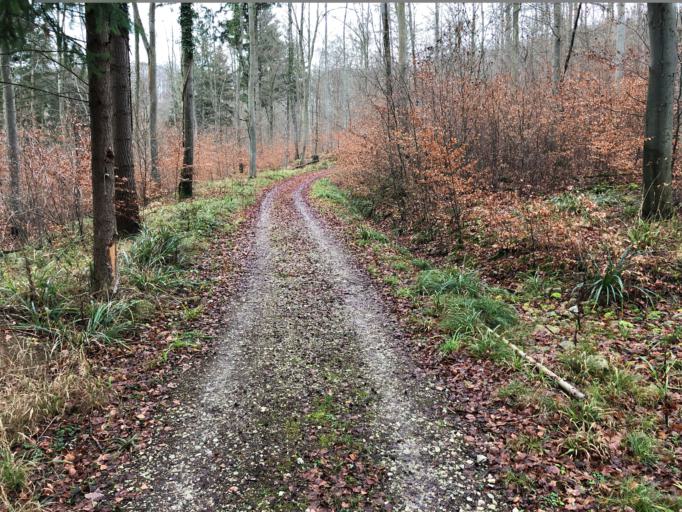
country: DE
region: Baden-Wuerttemberg
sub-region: Tuebingen Region
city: Nehren
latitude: 48.4185
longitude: 9.0851
